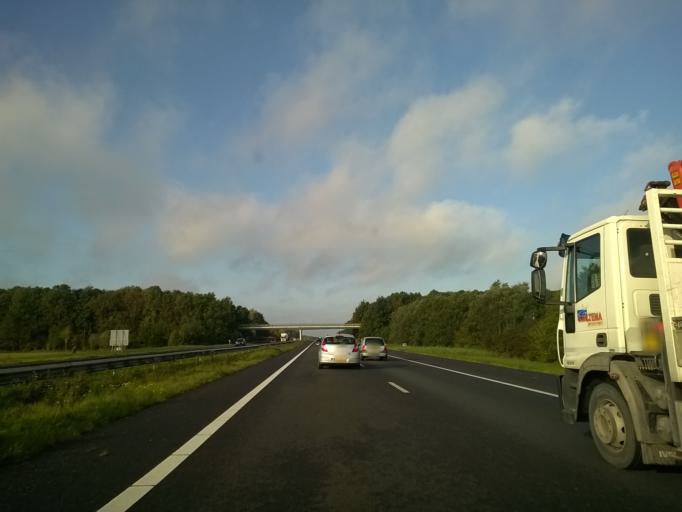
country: NL
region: Groningen
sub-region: Gemeente Zuidhorn
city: Zuidhorn
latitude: 53.1950
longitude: 6.4271
